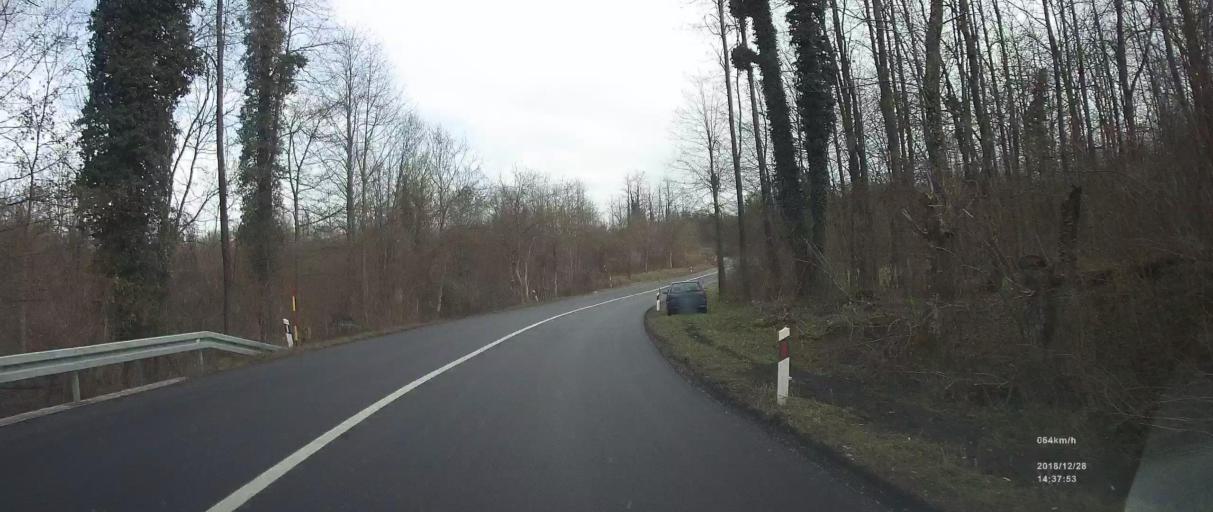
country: HR
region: Primorsko-Goranska
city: Vrbovsko
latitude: 45.4222
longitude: 15.2154
